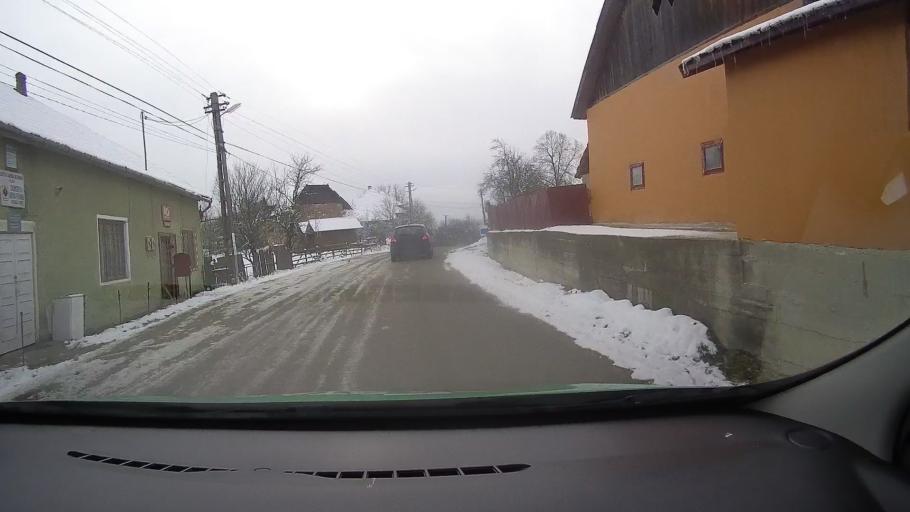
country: RO
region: Alba
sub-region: Comuna Almasu Mare
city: Almasu Mare
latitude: 46.0885
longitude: 23.1297
